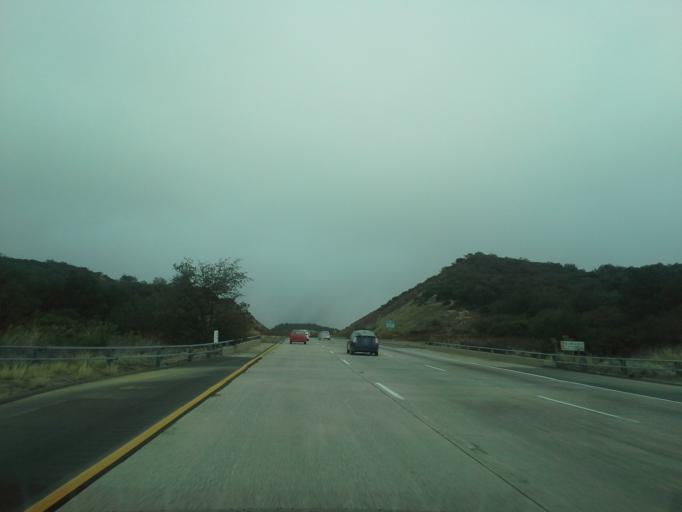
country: US
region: California
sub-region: San Diego County
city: Pine Valley
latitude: 32.8192
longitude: -116.5773
